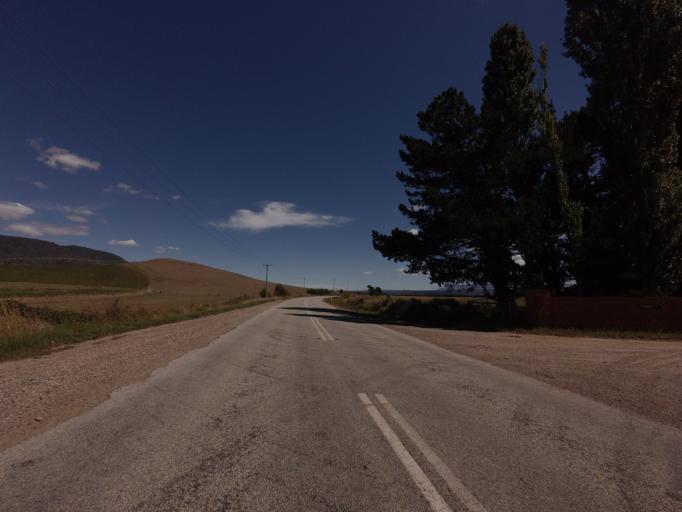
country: AU
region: Tasmania
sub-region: Break O'Day
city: St Helens
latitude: -41.5998
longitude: 148.0446
